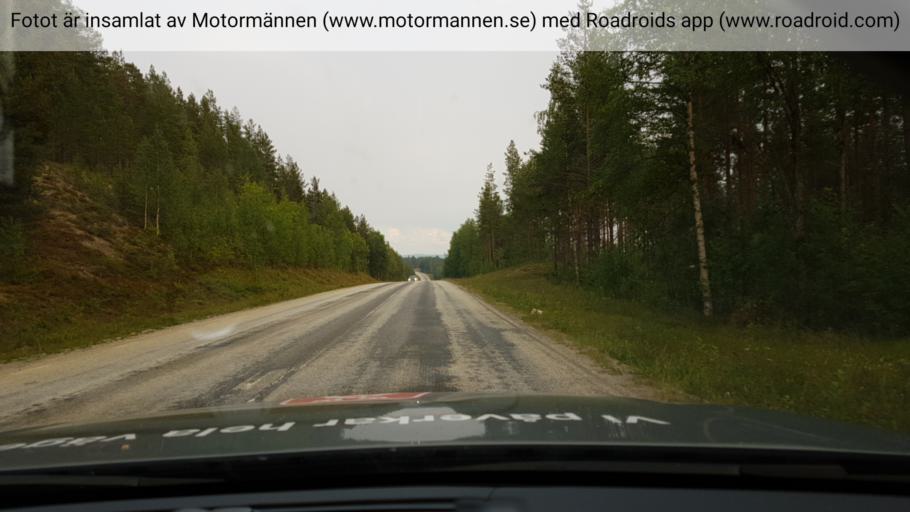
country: SE
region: Jaemtland
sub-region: Harjedalens Kommun
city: Sveg
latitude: 62.4198
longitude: 13.5414
